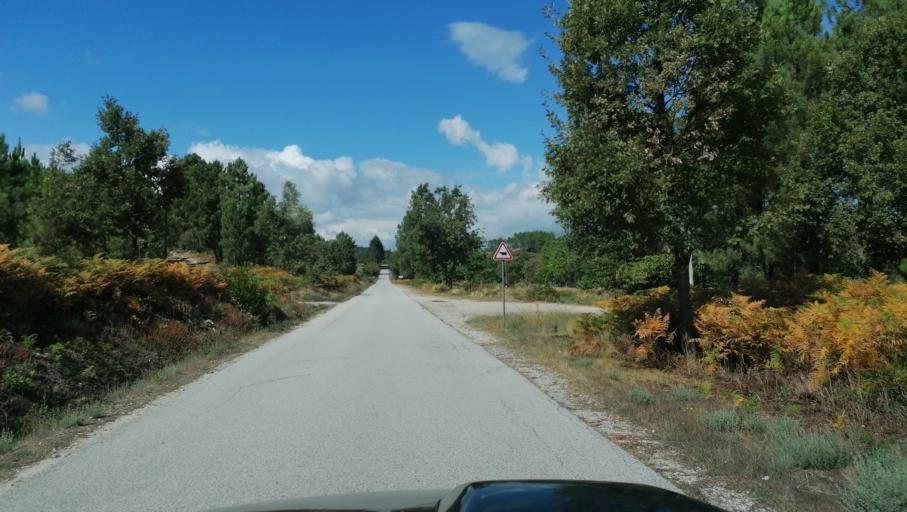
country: PT
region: Vila Real
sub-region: Vila Pouca de Aguiar
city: Vila Pouca de Aguiar
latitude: 41.5561
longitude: -7.6389
